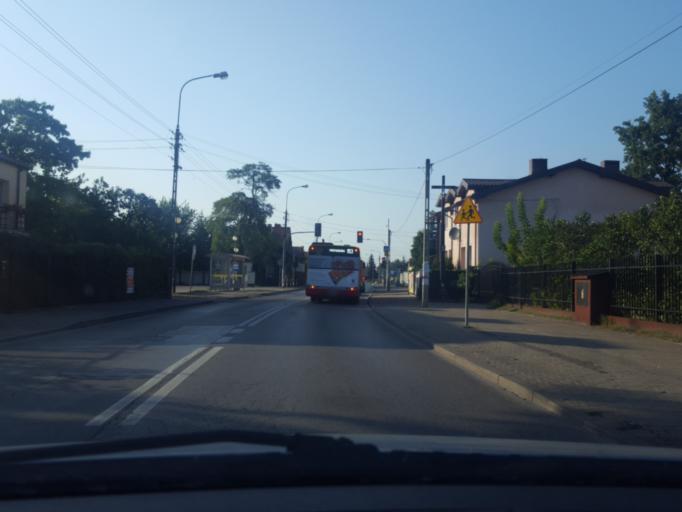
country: PL
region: Masovian Voivodeship
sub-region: Warszawa
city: Rembertow
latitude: 52.2628
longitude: 21.1576
